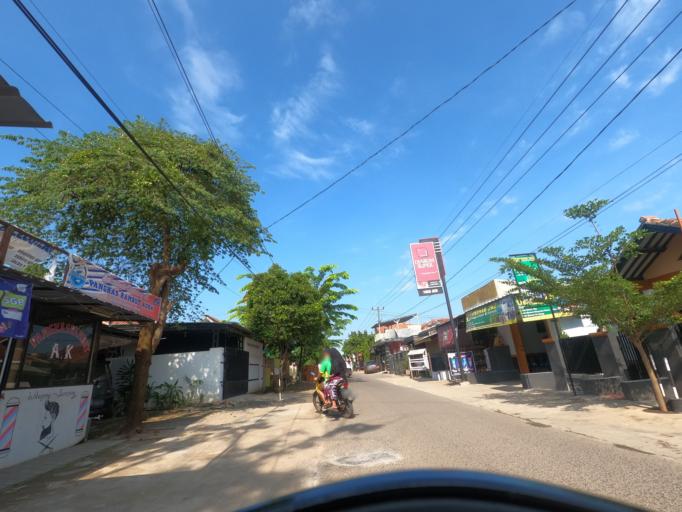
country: ID
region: West Java
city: Lembang
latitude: -6.5783
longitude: 107.7856
